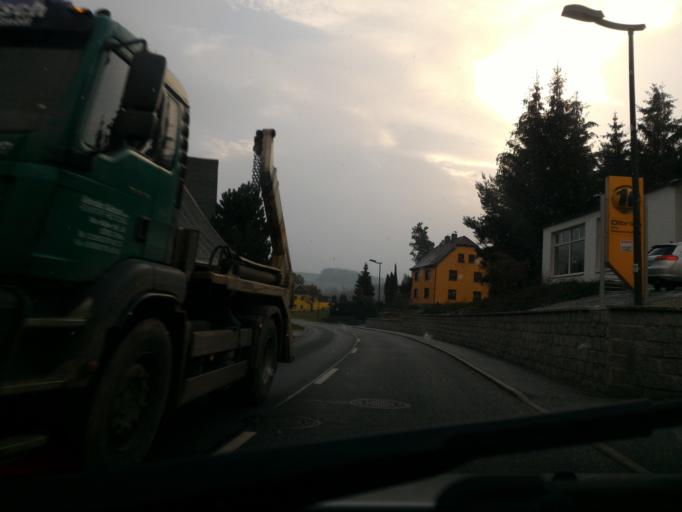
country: DE
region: Saxony
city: Grossschonau
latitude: 50.8925
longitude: 14.6797
